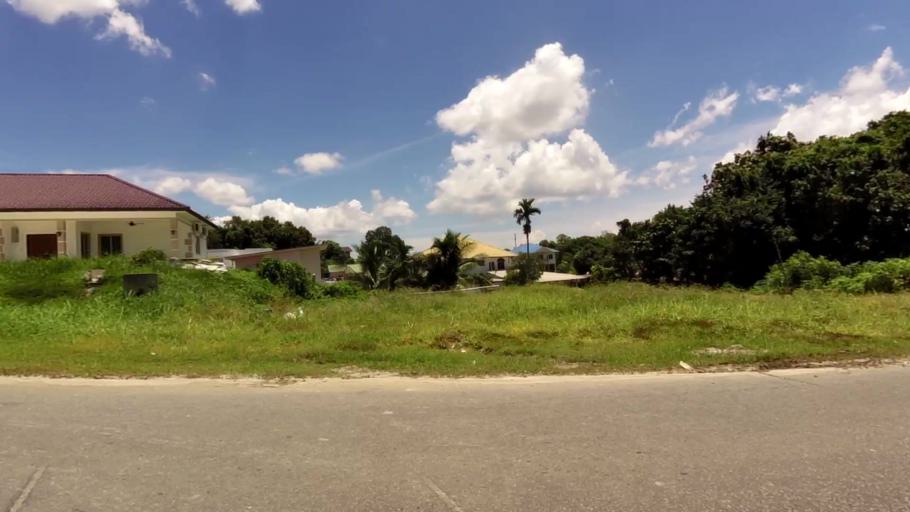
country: BN
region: Brunei and Muara
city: Bandar Seri Begawan
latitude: 4.9377
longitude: 114.9591
